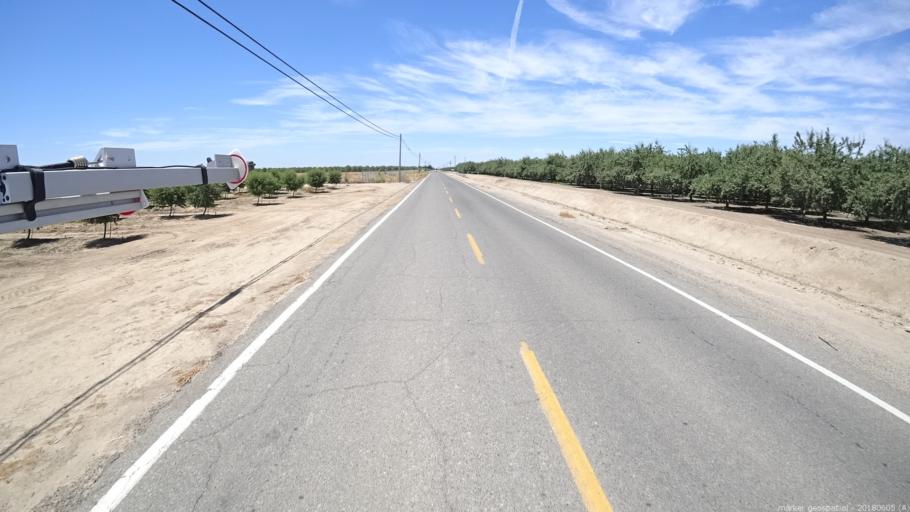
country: US
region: California
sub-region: Madera County
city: Chowchilla
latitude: 37.1127
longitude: -120.2990
